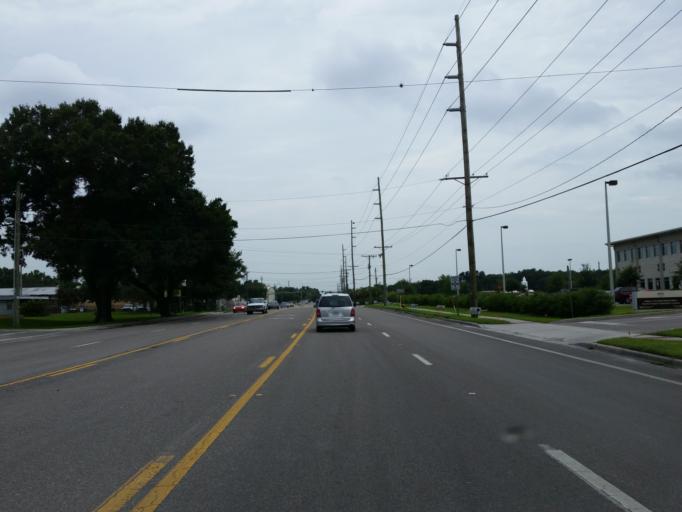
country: US
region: Florida
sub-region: Hillsborough County
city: Mango
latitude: 27.9551
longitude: -82.3352
